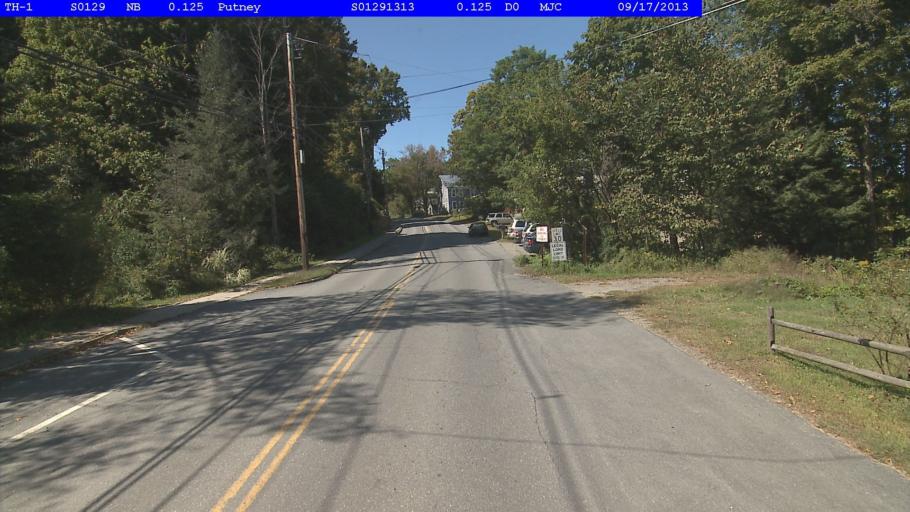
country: US
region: New Hampshire
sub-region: Cheshire County
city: Westmoreland
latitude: 42.9762
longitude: -72.5237
